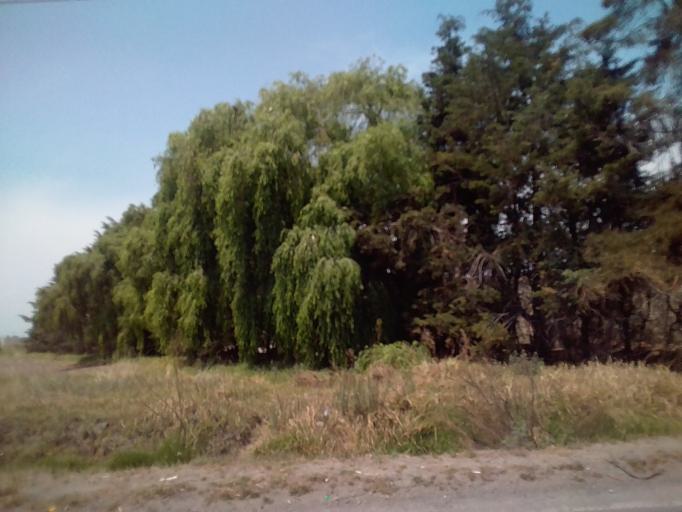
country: MX
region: Mexico
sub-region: Toluca
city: San Nicolas Tolentino
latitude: 19.3621
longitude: -99.5617
